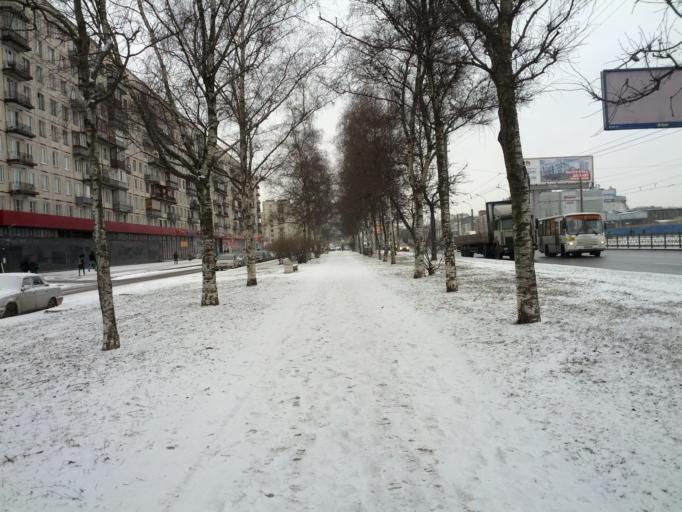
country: RU
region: Leningrad
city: Rybatskoye
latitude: 59.9040
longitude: 30.4848
